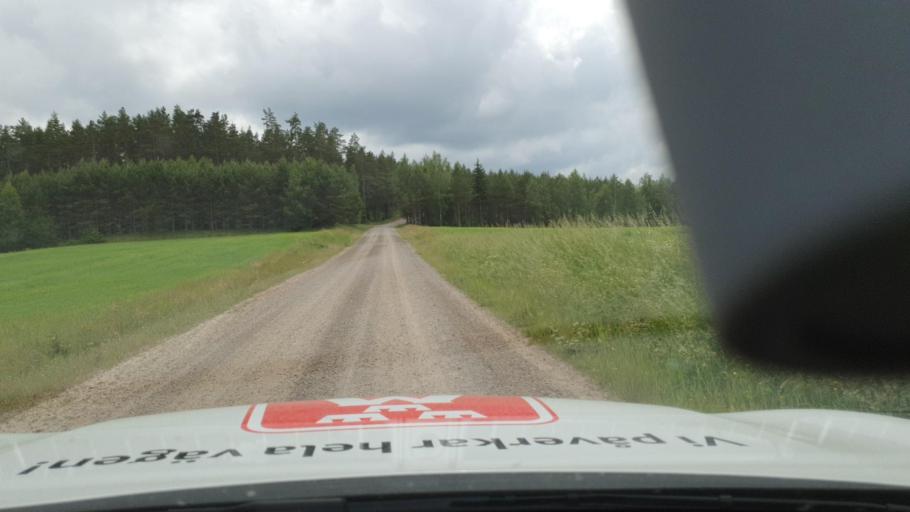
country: SE
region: Vaestra Goetaland
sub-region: Tidaholms Kommun
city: Olofstorp
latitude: 58.2125
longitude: 14.1102
